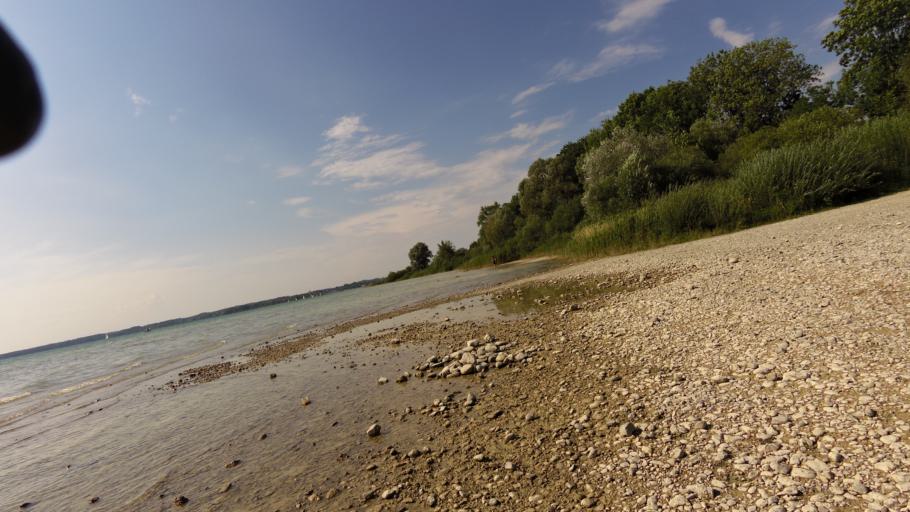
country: DE
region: Bavaria
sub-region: Upper Bavaria
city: Chieming
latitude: 47.9149
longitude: 12.4969
